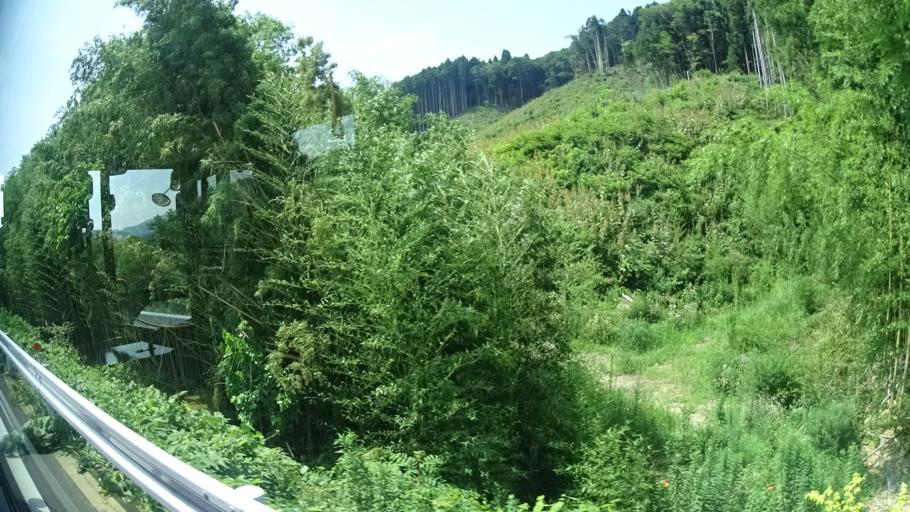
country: JP
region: Miyagi
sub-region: Oshika Gun
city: Onagawa Cho
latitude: 38.6471
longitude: 141.4179
